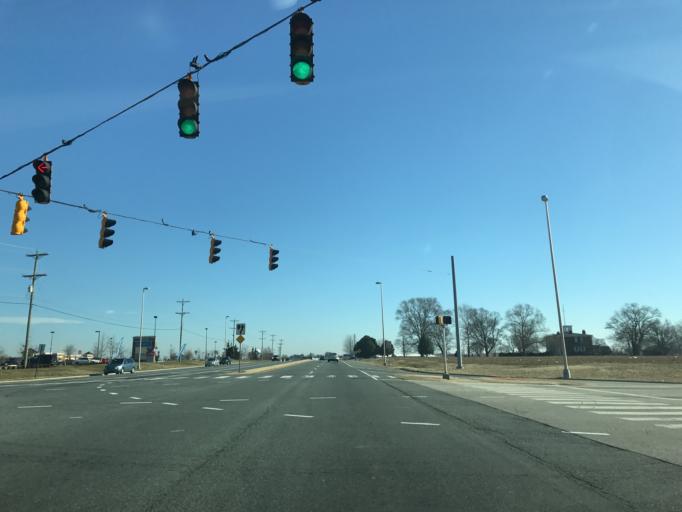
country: US
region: Delaware
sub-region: New Castle County
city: Middletown
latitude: 39.4434
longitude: -75.7394
